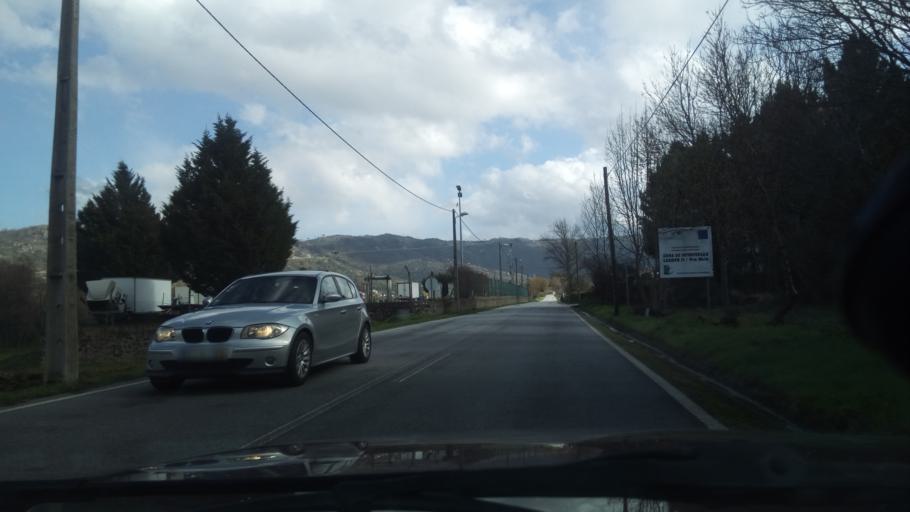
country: PT
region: Guarda
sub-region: Celorico da Beira
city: Celorico da Beira
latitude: 40.6174
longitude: -7.3093
